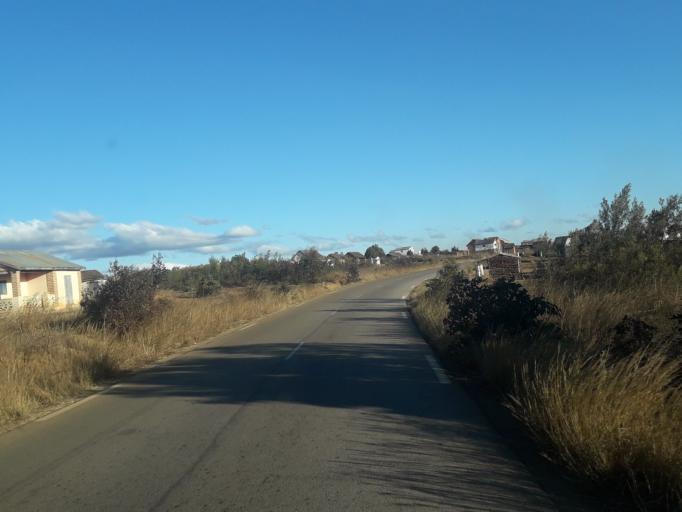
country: MG
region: Analamanga
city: Ankazobe
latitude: -18.1355
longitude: 47.2275
